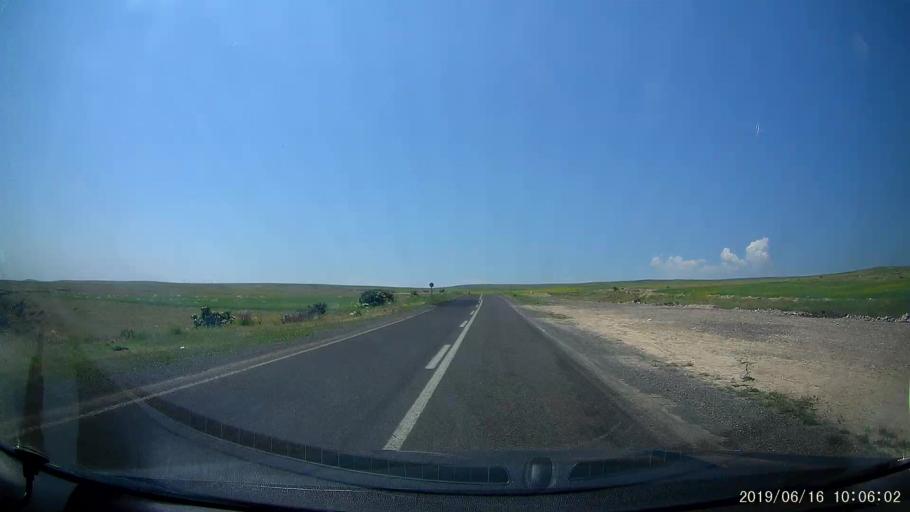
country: TR
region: Kars
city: Digor
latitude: 40.2613
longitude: 43.5407
